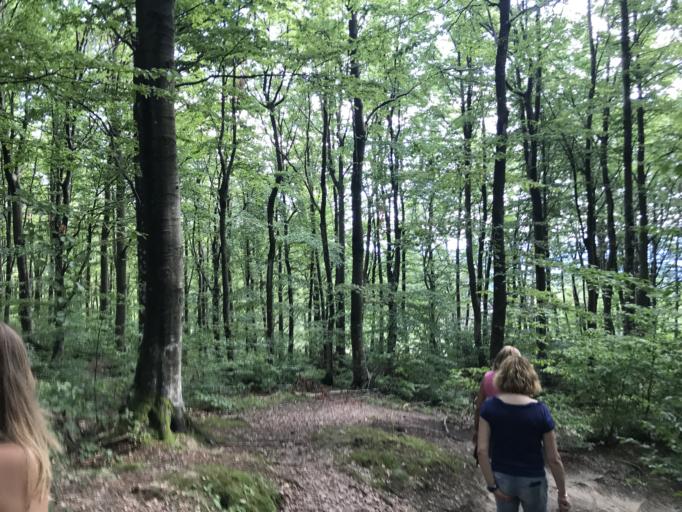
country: IT
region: Emilia-Romagna
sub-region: Provincia di Bologna
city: San Benedetto Val di Sambro
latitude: 44.1551
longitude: 11.2623
